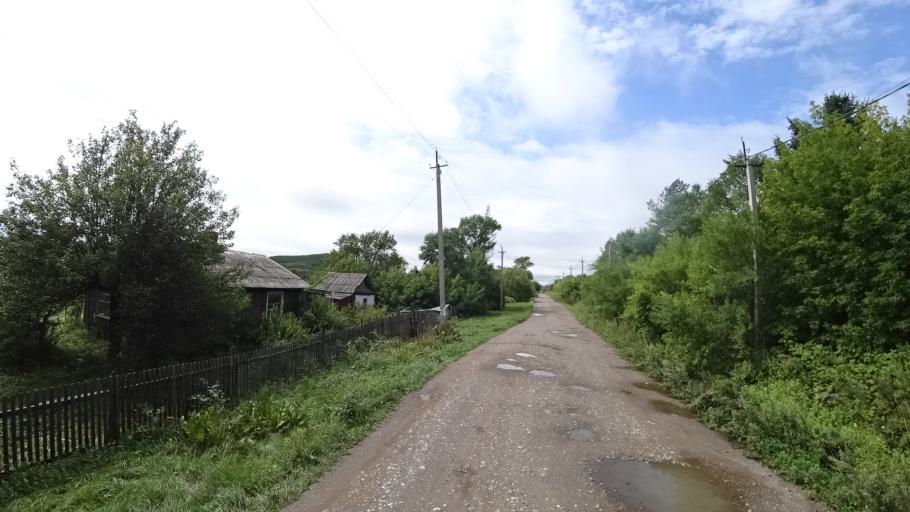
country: RU
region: Primorskiy
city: Lyalichi
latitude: 44.1391
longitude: 132.3815
